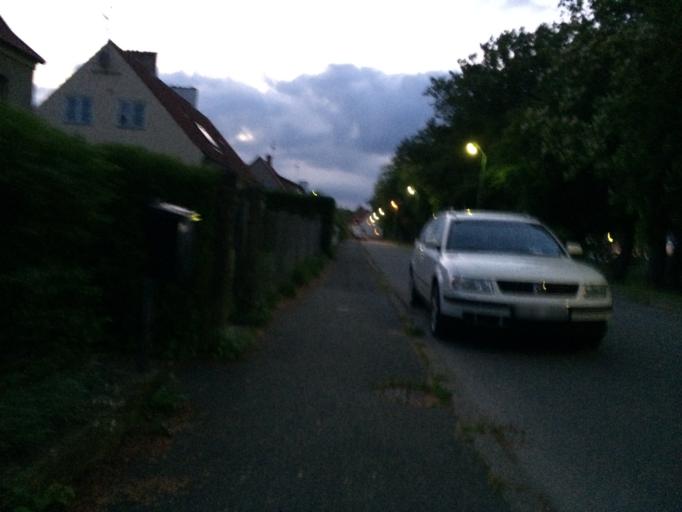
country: SE
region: Skane
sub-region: Simrishamns Kommun
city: Simrishamn
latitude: 55.5586
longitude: 14.3431
